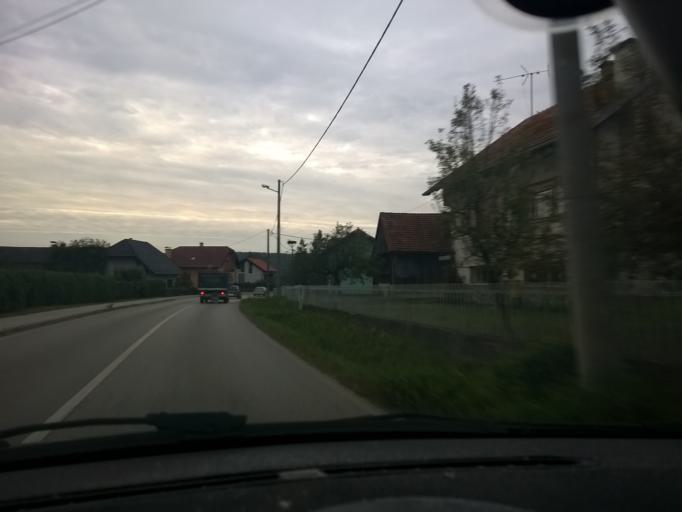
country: HR
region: Zagrebacka
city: Pojatno
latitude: 45.9037
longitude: 15.8018
